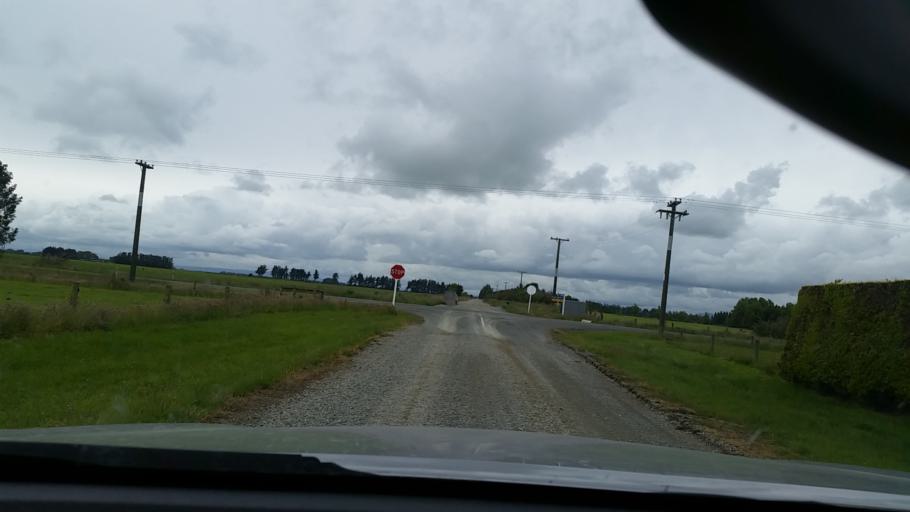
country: NZ
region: Southland
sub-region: Southland District
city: Winton
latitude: -46.2525
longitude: 168.3673
